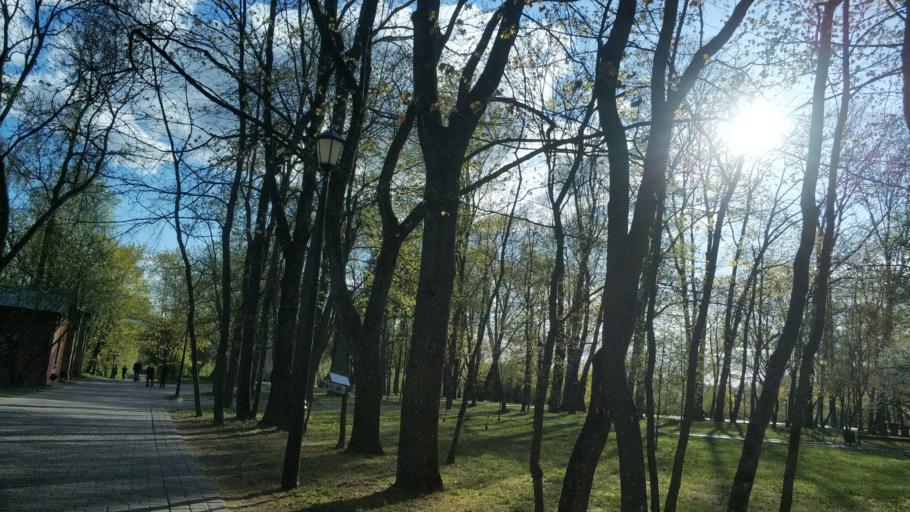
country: BY
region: Minsk
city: Minsk
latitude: 53.8531
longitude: 27.5776
